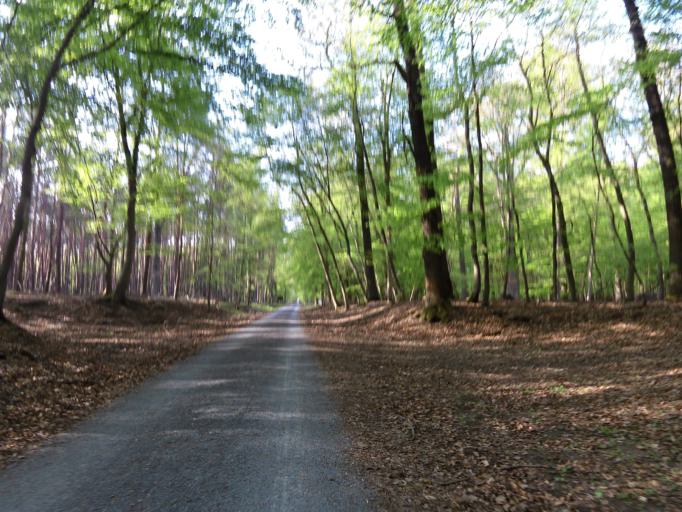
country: DE
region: Hesse
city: Raunheim
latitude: 49.9898
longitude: 8.5005
